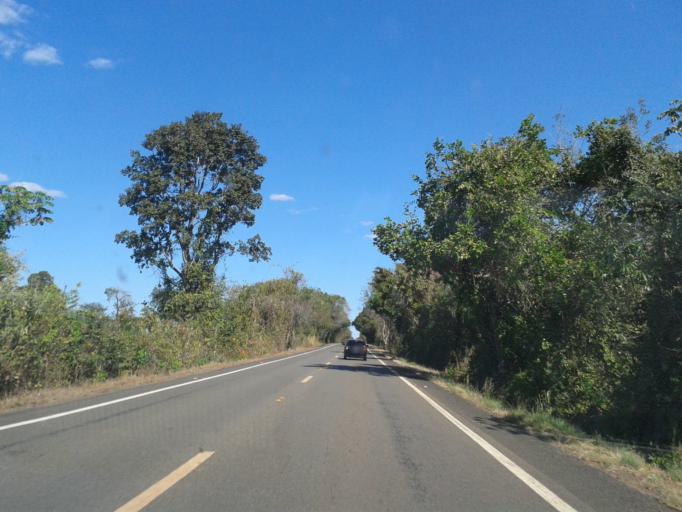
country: BR
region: Goias
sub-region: Sao Miguel Do Araguaia
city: Sao Miguel do Araguaia
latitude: -13.8646
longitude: -50.3335
